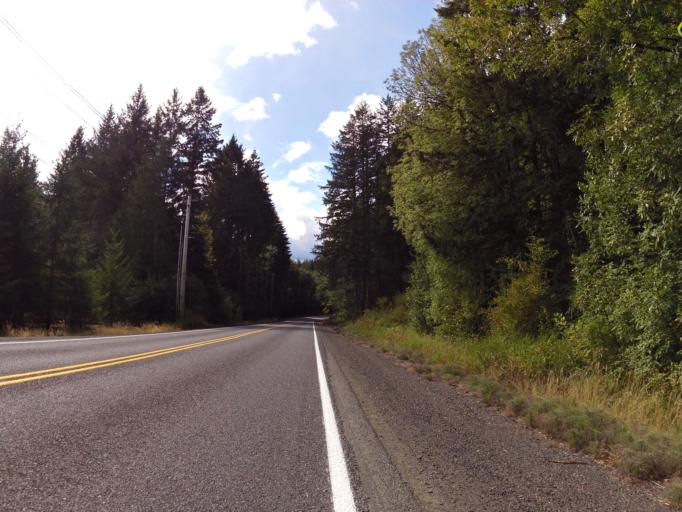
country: US
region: Washington
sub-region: Mason County
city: Shelton
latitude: 47.1511
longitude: -123.0619
